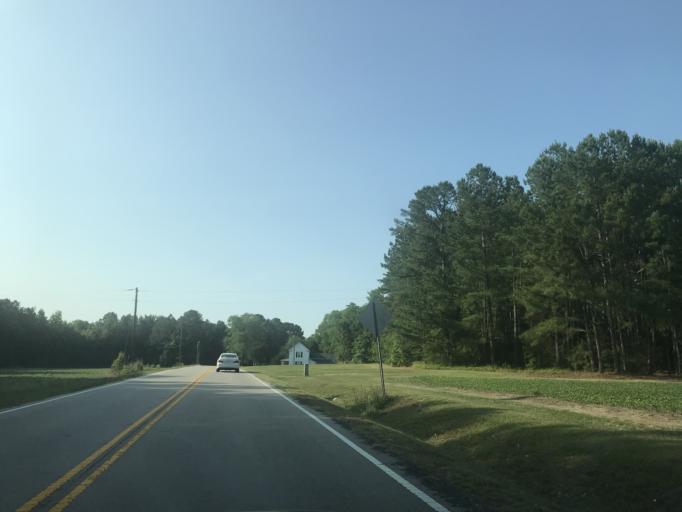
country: US
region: North Carolina
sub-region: Wake County
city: Knightdale
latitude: 35.8415
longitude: -78.5012
